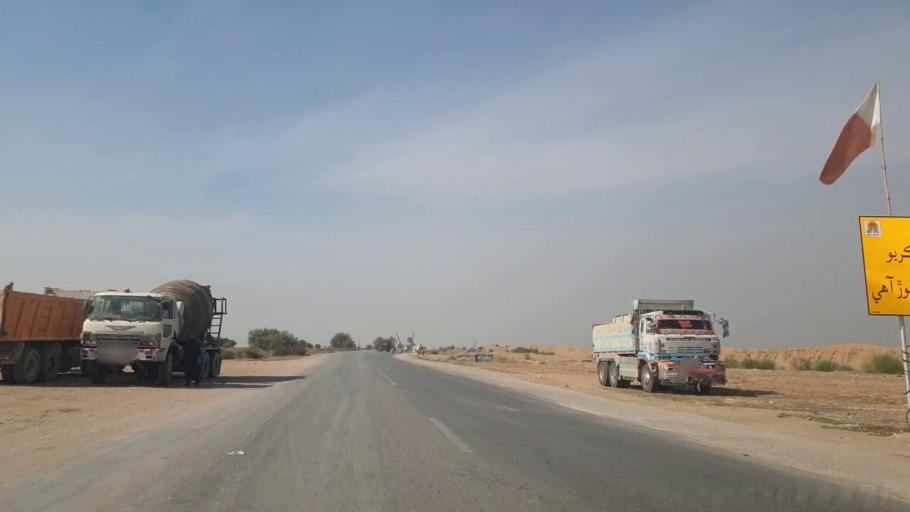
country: PK
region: Sindh
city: Sann
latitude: 26.0287
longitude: 68.1244
